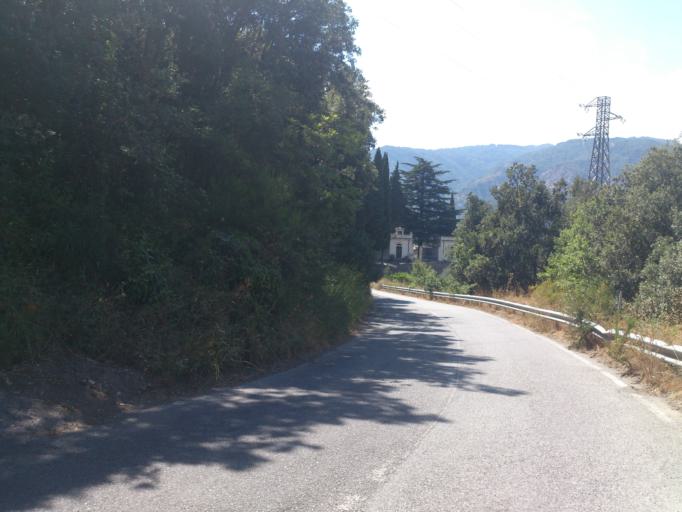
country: IT
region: Calabria
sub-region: Provincia di Reggio Calabria
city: Pazzano
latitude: 38.4756
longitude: 16.4478
